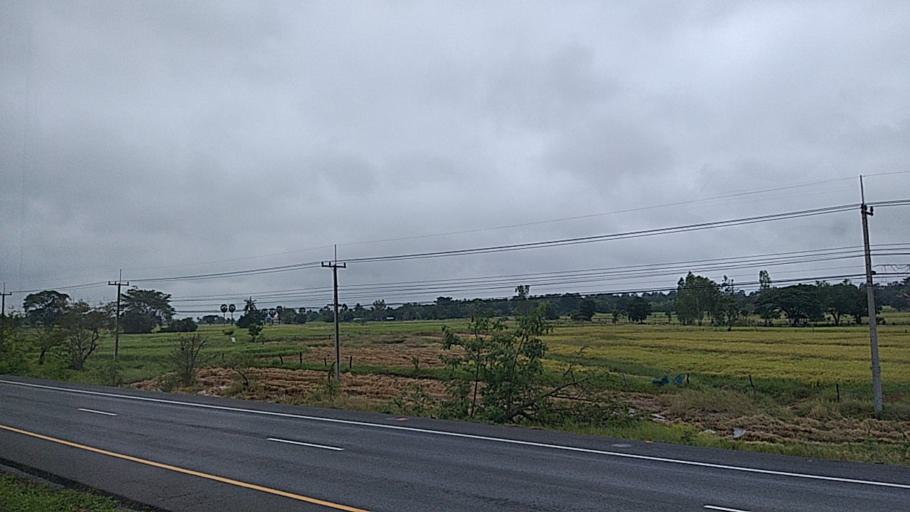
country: TH
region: Nakhon Ratchasima
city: Non Daeng
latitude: 15.3873
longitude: 102.4661
